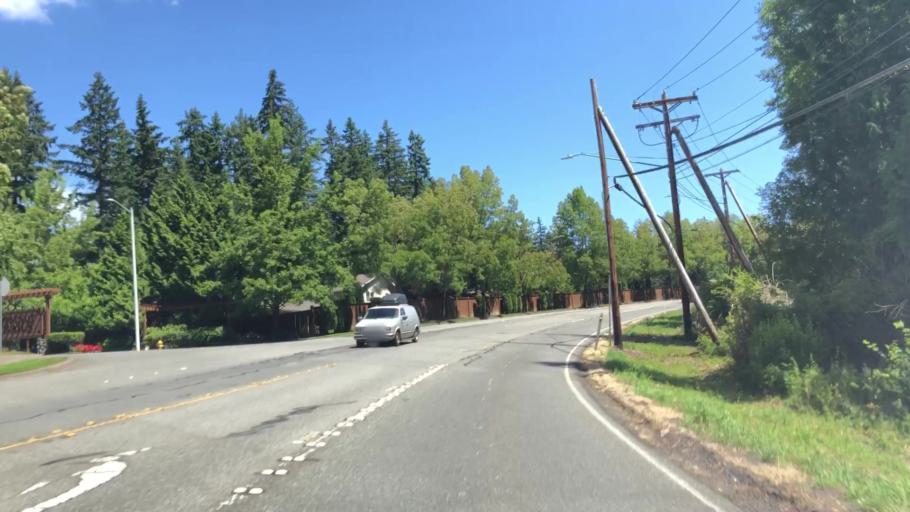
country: US
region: Washington
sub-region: Snohomish County
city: North Creek
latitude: 47.8143
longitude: -122.1900
